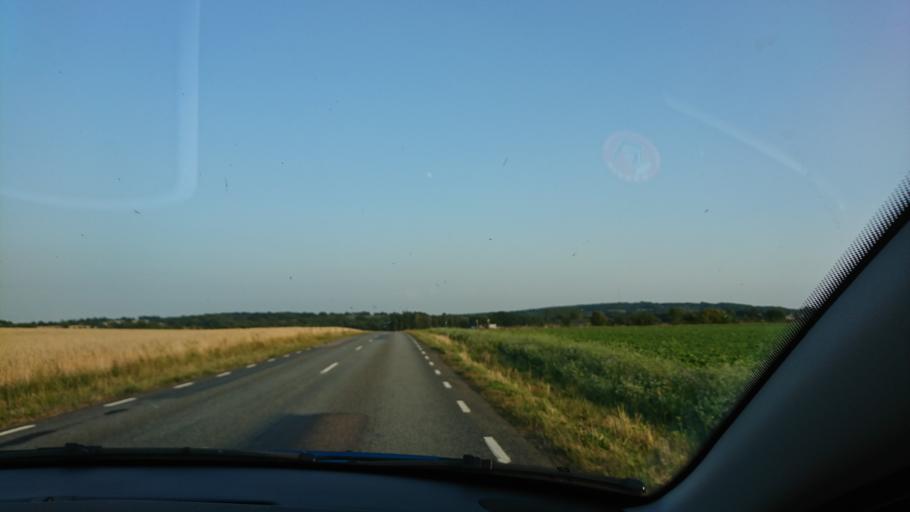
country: SE
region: Skane
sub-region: Simrishamns Kommun
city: Kivik
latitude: 55.6950
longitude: 14.1558
